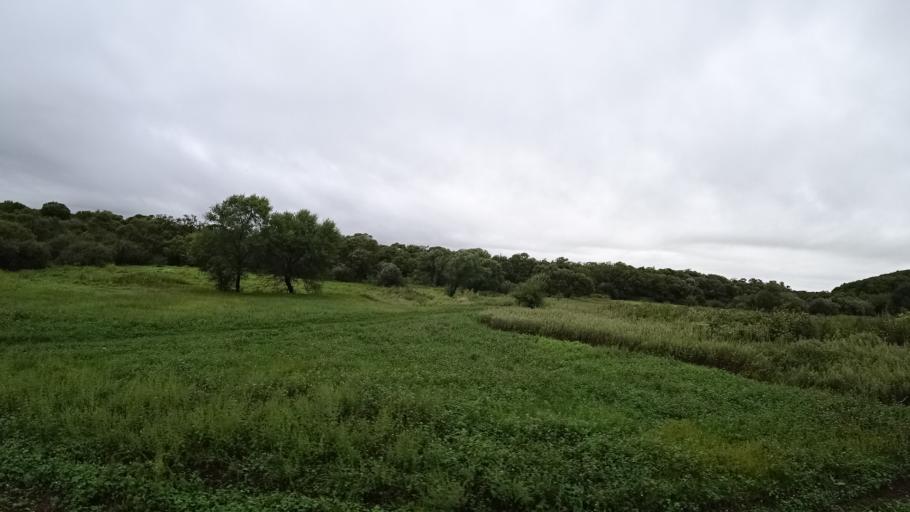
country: RU
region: Primorskiy
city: Monastyrishche
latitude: 44.2713
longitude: 132.4049
